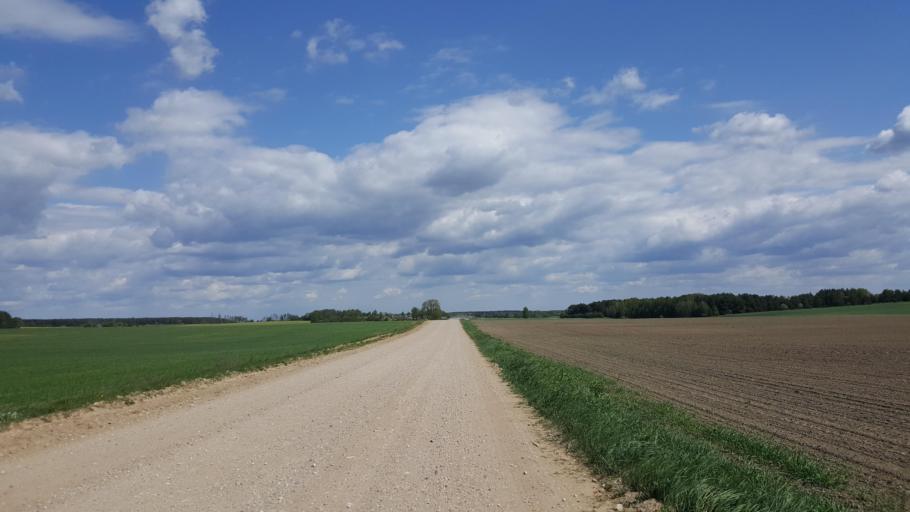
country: BY
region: Brest
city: Kamyanyets
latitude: 52.3774
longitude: 23.8792
